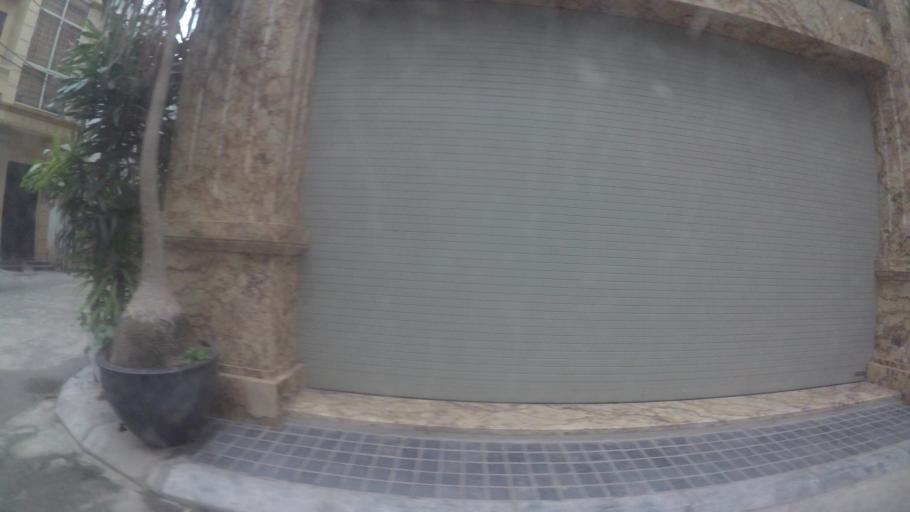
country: VN
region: Ha Noi
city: Cau Dien
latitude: 21.0331
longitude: 105.7822
